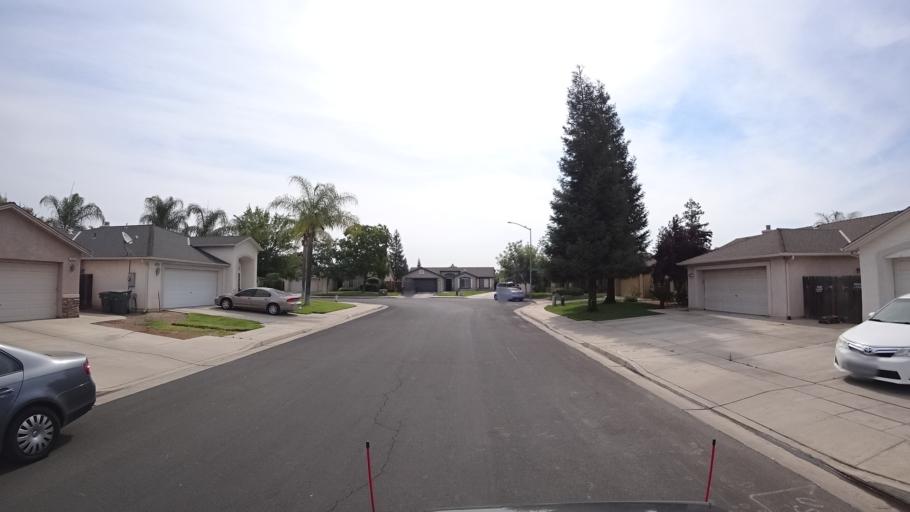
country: US
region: California
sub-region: Fresno County
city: West Park
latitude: 36.7625
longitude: -119.8913
